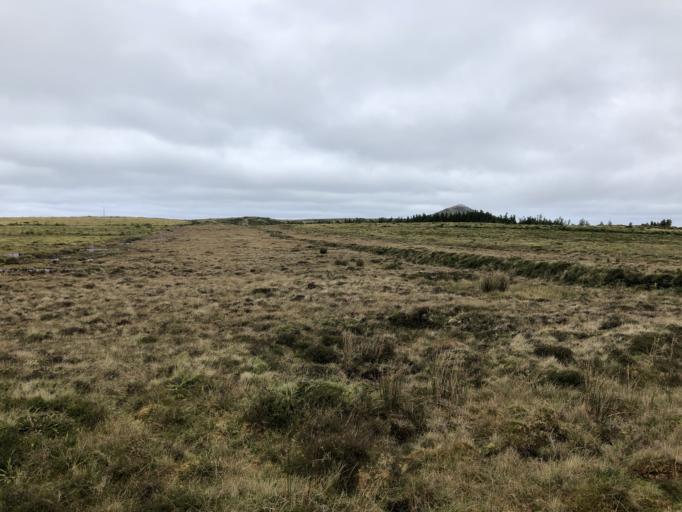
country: PT
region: Azores
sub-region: Povoacao
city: Furnas
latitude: 37.7994
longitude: -25.2406
